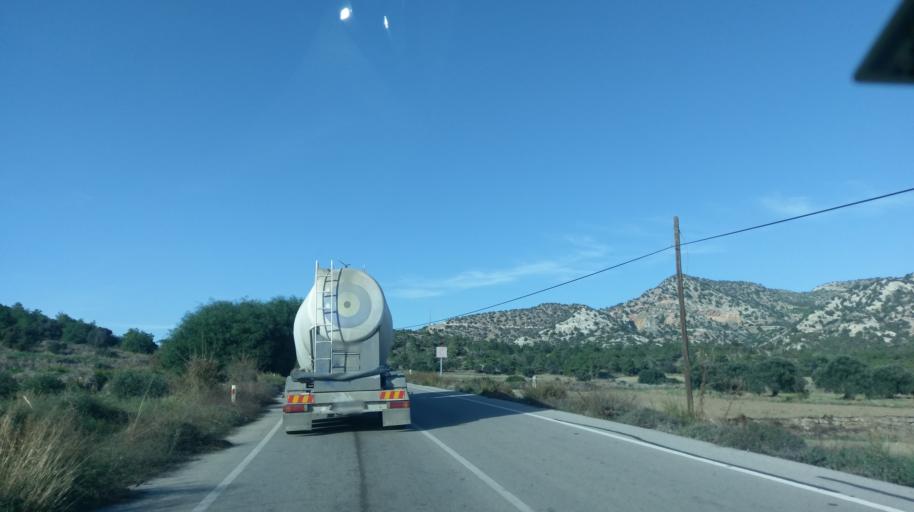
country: CY
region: Ammochostos
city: Lefkonoiko
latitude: 35.3350
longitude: 33.7200
